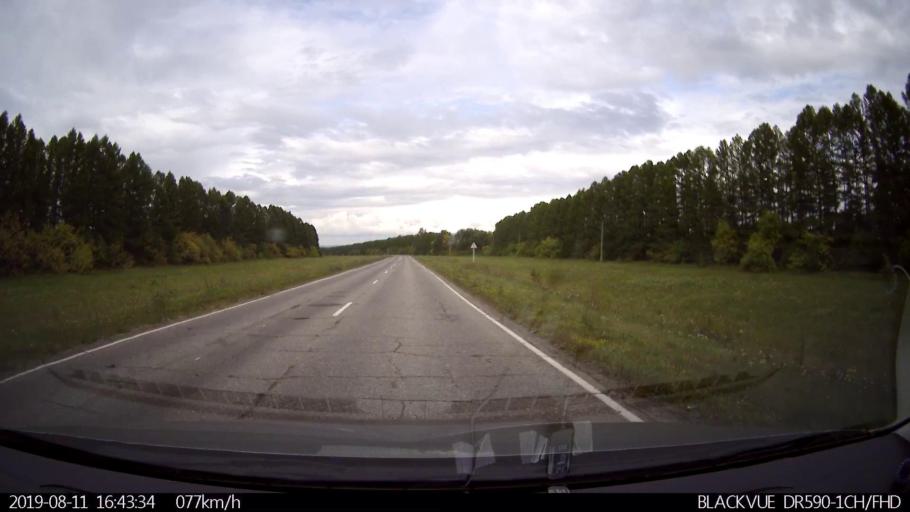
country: RU
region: Ulyanovsk
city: Mayna
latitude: 54.1704
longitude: 47.6736
